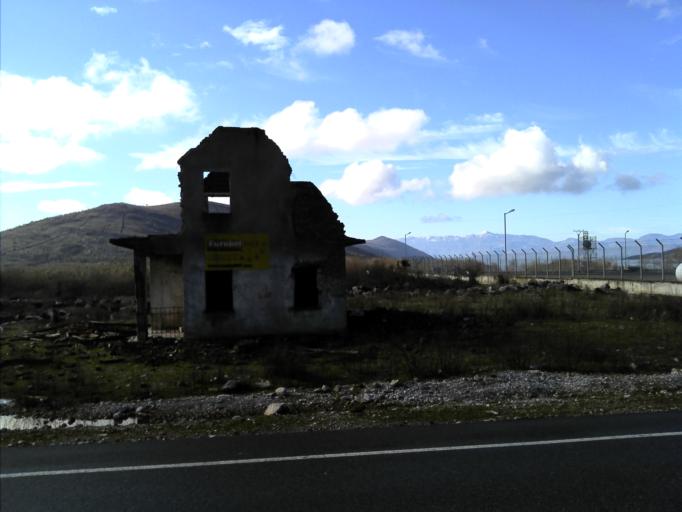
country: AL
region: Shkoder
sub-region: Rrethi i Malesia e Madhe
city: Hot
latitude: 42.3365
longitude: 19.4338
